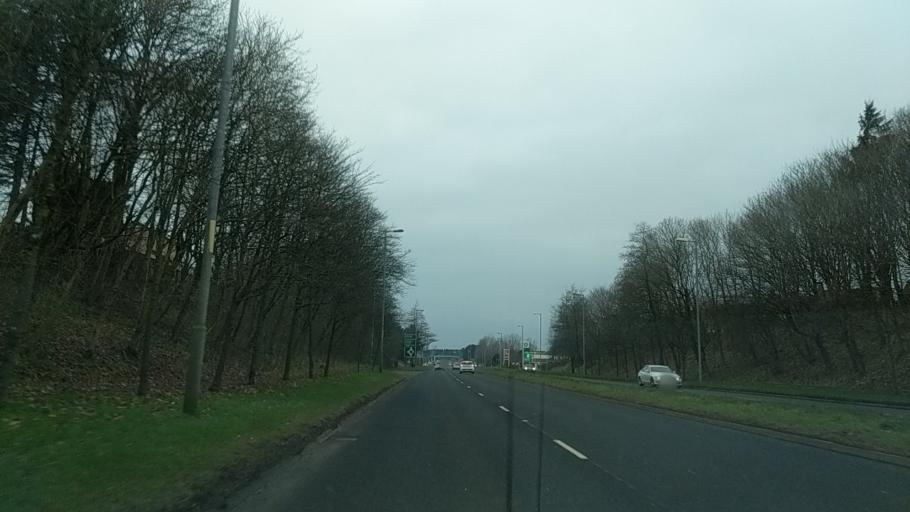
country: GB
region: Scotland
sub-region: South Lanarkshire
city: East Kilbride
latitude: 55.7634
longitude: -4.2020
